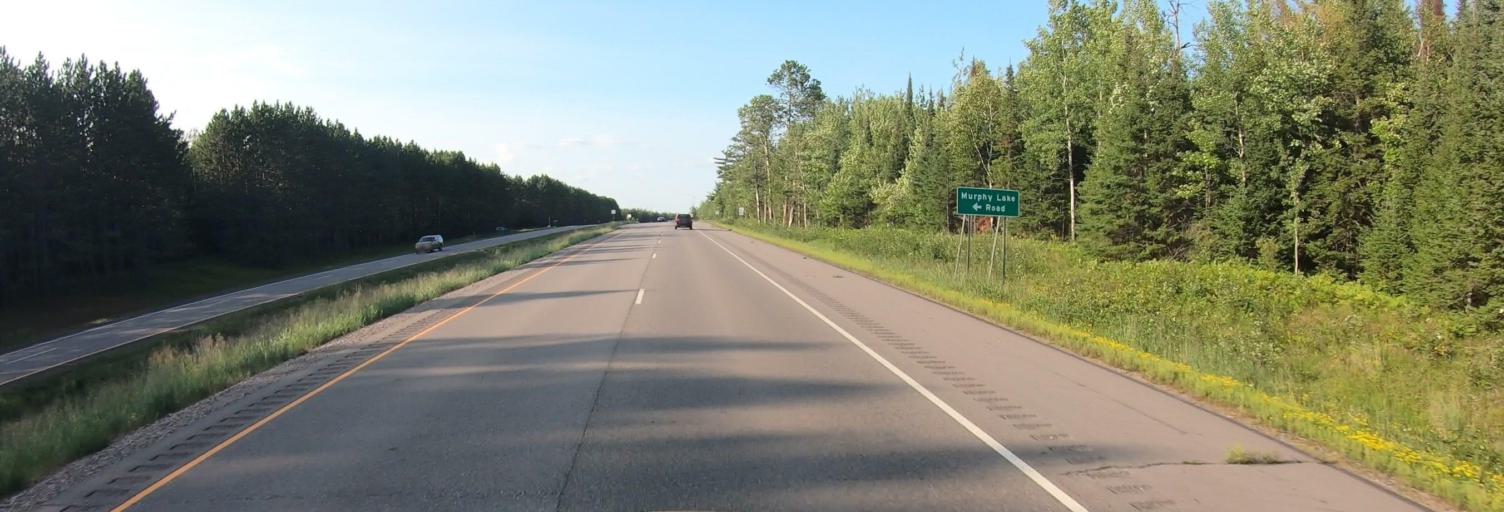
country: US
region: Minnesota
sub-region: Saint Louis County
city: Eveleth
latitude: 47.3042
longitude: -92.4769
